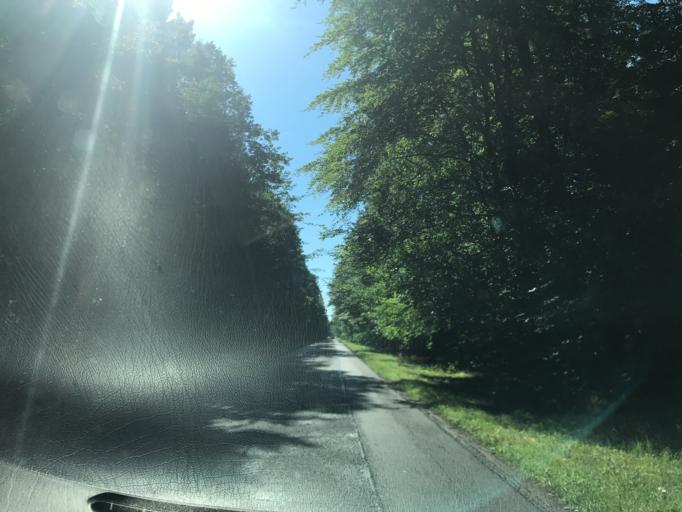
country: PL
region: Pomeranian Voivodeship
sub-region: Powiat bytowski
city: Czarna Dabrowka
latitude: 54.3838
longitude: 17.4842
